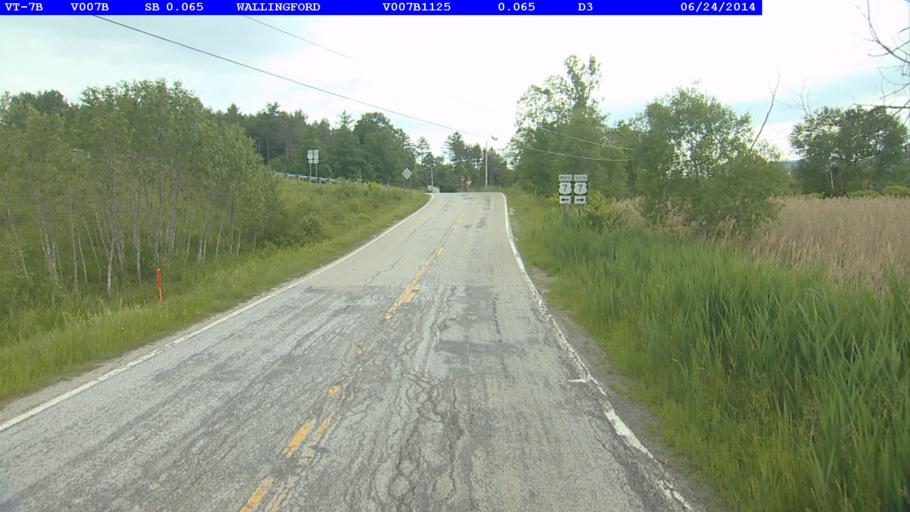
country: US
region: Vermont
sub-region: Rutland County
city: Rutland
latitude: 43.4850
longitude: -72.9732
